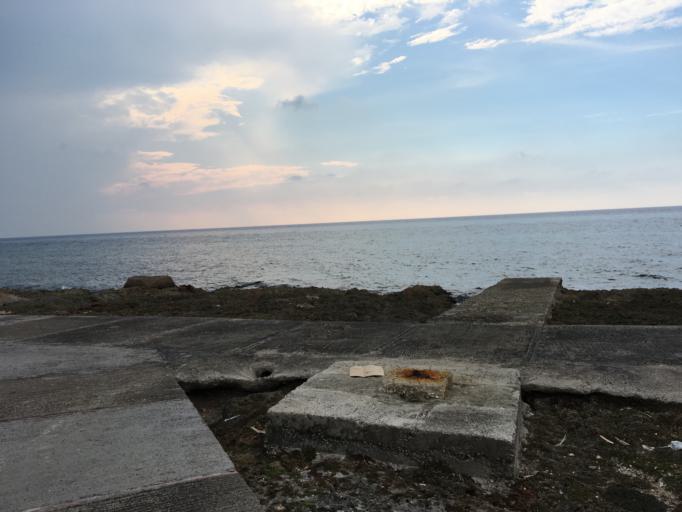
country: CU
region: La Habana
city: Havana
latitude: 23.1137
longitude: -82.4399
